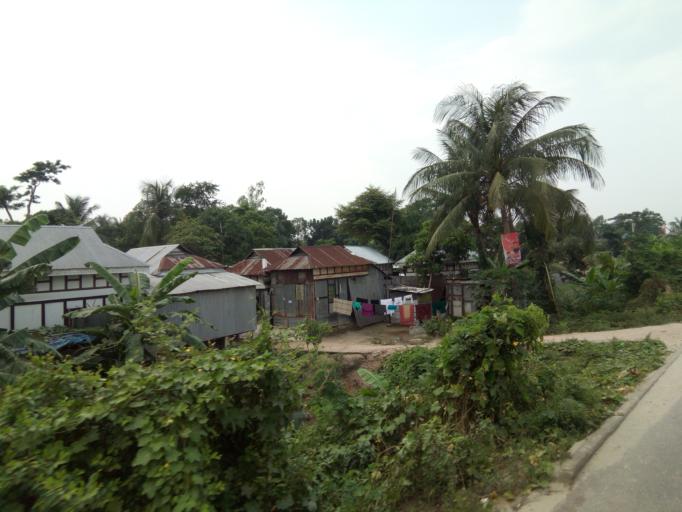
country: BD
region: Dhaka
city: Dohar
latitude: 23.5501
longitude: 90.3000
